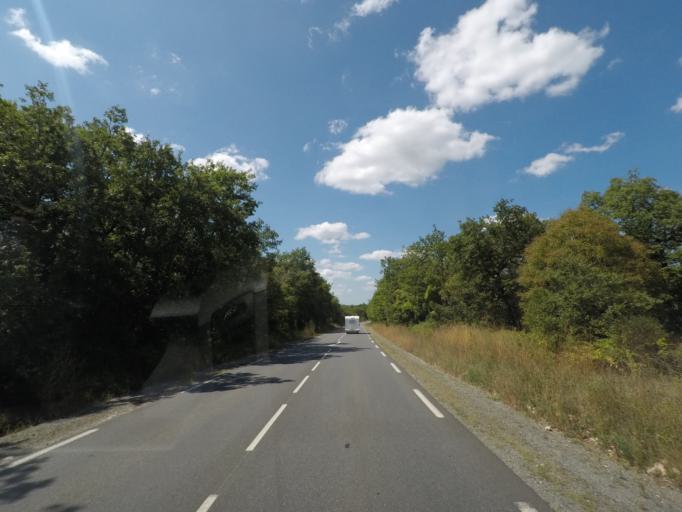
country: FR
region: Midi-Pyrenees
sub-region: Departement du Lot
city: Lacapelle-Marival
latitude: 44.6217
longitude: 1.9179
